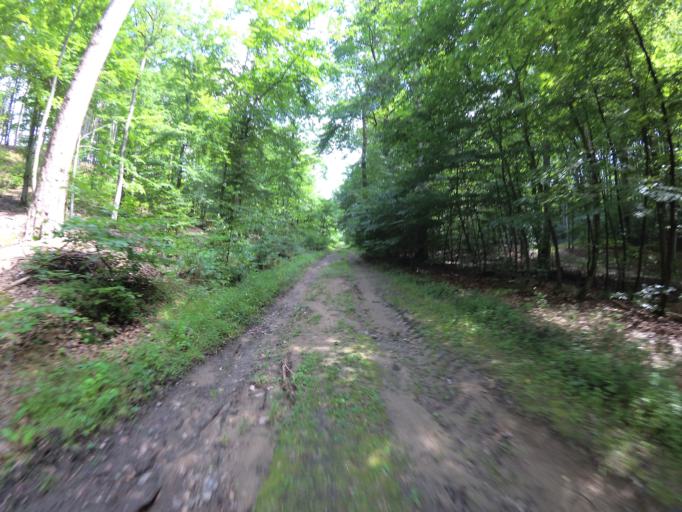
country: PL
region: Pomeranian Voivodeship
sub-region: Gdynia
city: Wielki Kack
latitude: 54.5100
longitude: 18.4746
